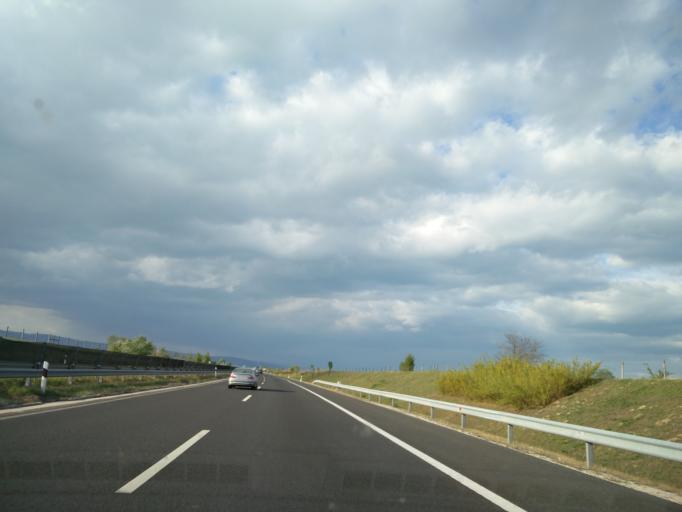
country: HU
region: Somogy
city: Zamardi
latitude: 46.8623
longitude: 17.9662
